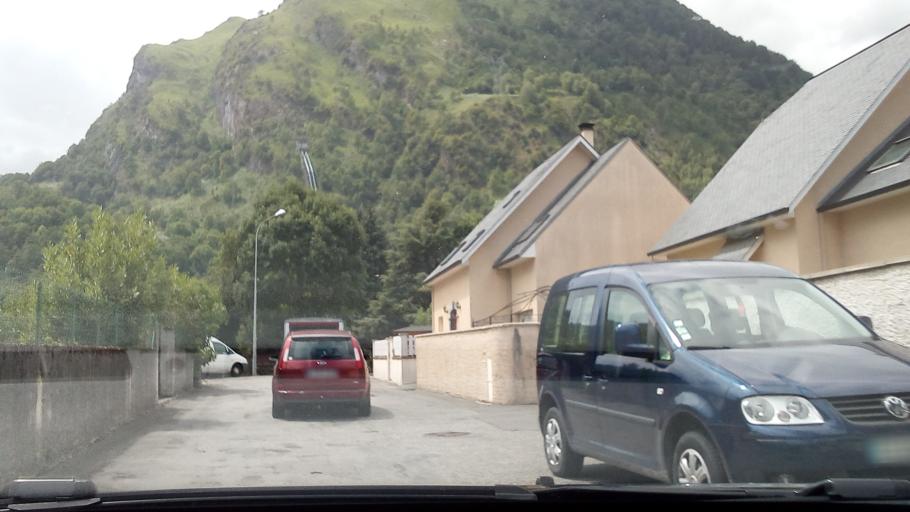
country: FR
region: Aquitaine
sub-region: Departement des Pyrenees-Atlantiques
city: Laruns
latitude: 42.9858
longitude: -0.4239
